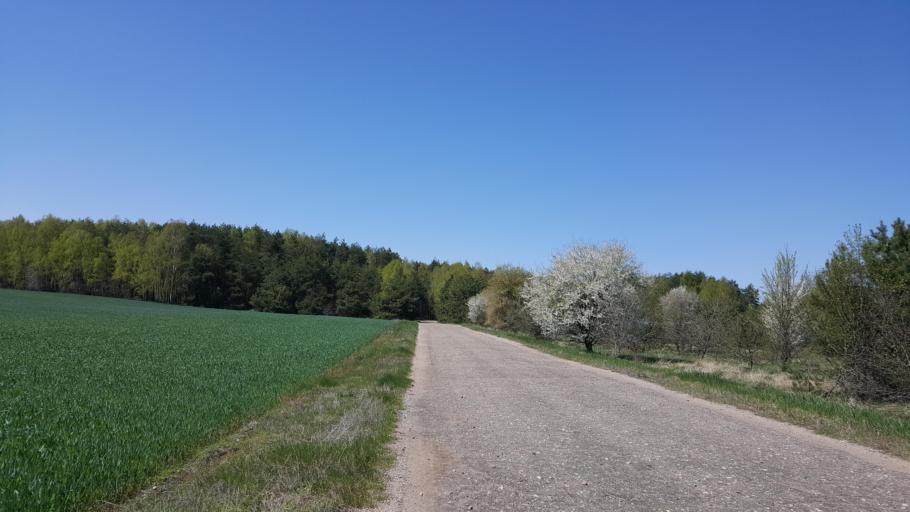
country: BY
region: Brest
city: Charnawchytsy
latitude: 52.3277
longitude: 23.6916
